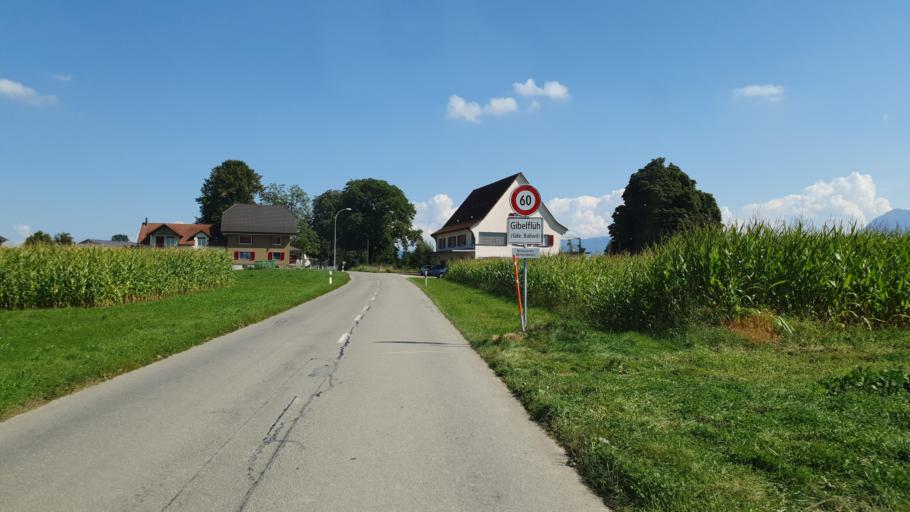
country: CH
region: Lucerne
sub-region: Hochdorf District
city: Inwil
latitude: 47.1488
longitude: 8.3487
